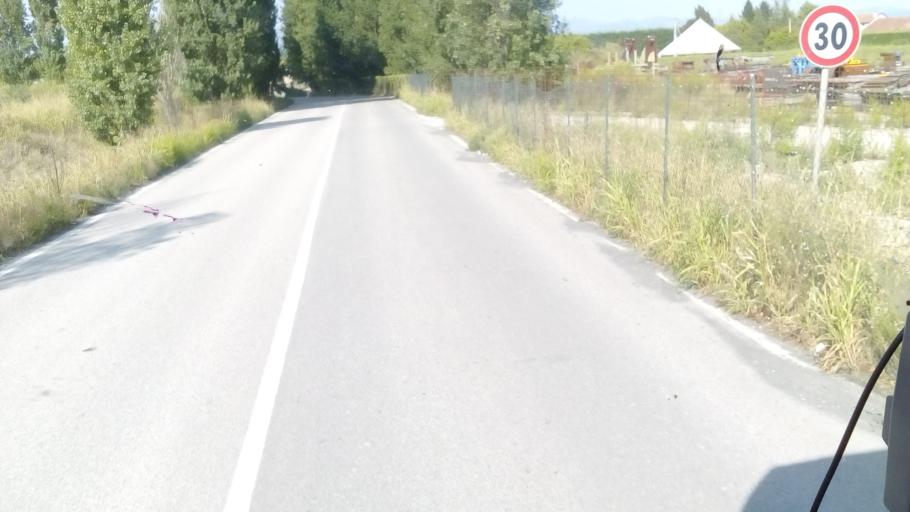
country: IT
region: Veneto
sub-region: Provincia di Verona
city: Campagnola
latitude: 45.3497
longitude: 11.0724
